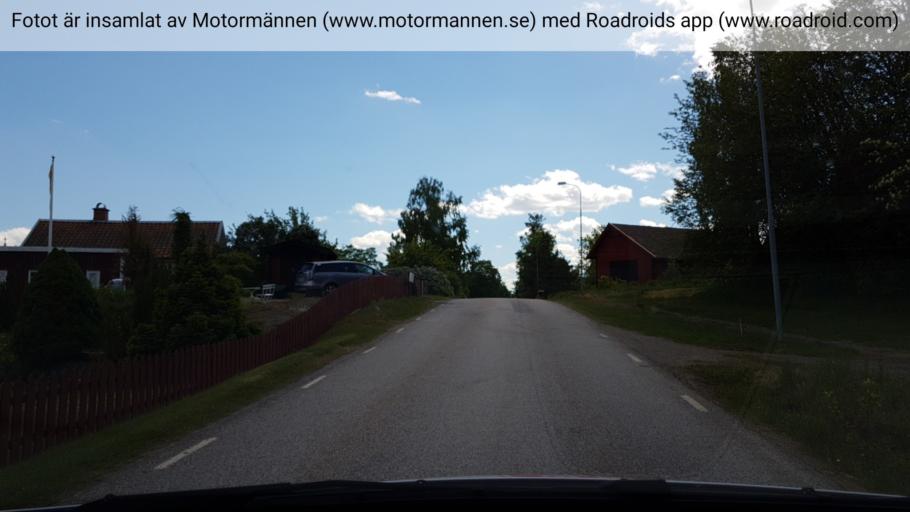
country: SE
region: Kalmar
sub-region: Vasterviks Kommun
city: Vaestervik
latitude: 57.9095
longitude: 16.6956
